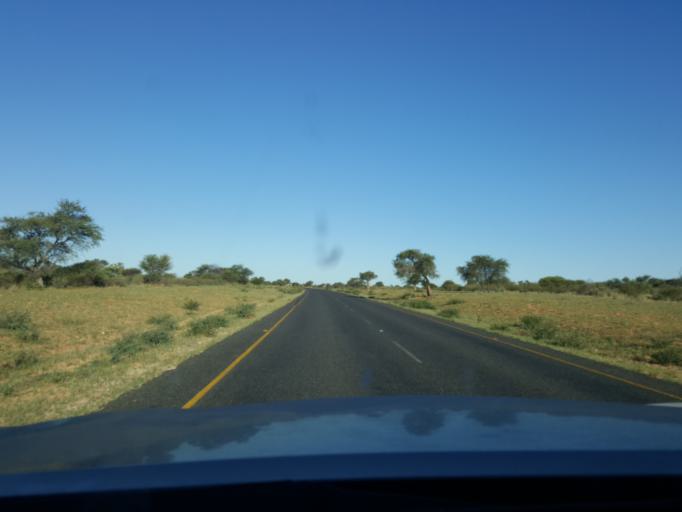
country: BW
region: Southern
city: Khakhea
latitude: -24.2255
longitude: 23.2386
